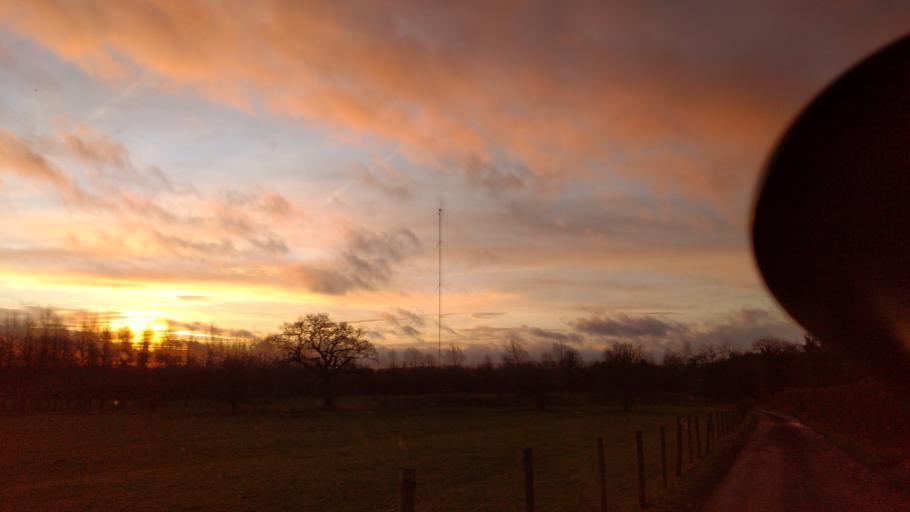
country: GB
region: England
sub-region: Borough of Swindon
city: Highworth
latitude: 51.5958
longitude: -1.6963
